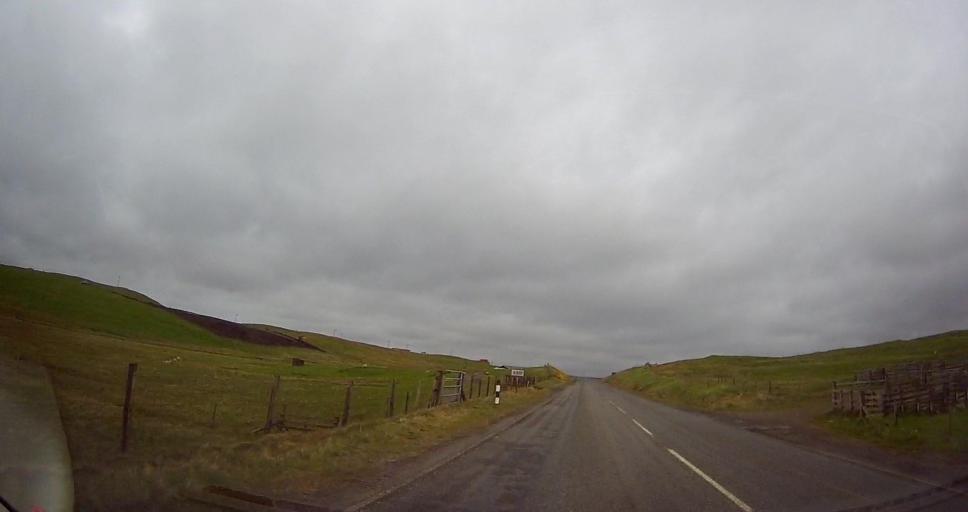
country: GB
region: Scotland
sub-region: Shetland Islands
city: Lerwick
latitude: 60.3740
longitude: -1.3370
